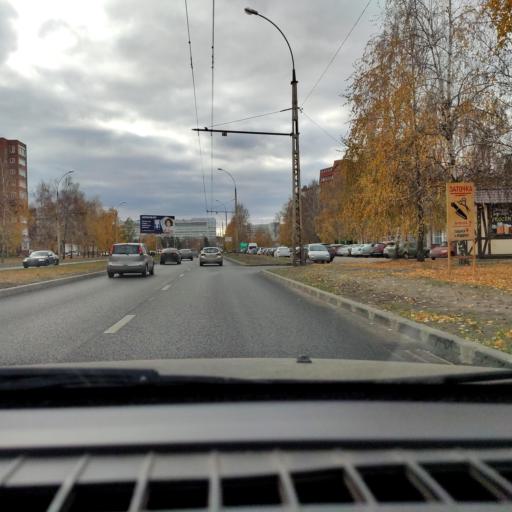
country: RU
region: Samara
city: Tol'yatti
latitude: 53.5284
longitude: 49.3272
